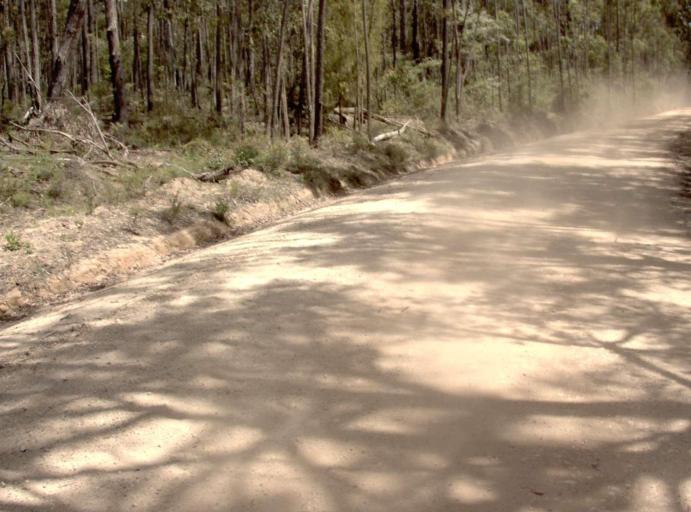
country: AU
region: Victoria
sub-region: East Gippsland
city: Lakes Entrance
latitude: -37.6422
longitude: 148.6625
